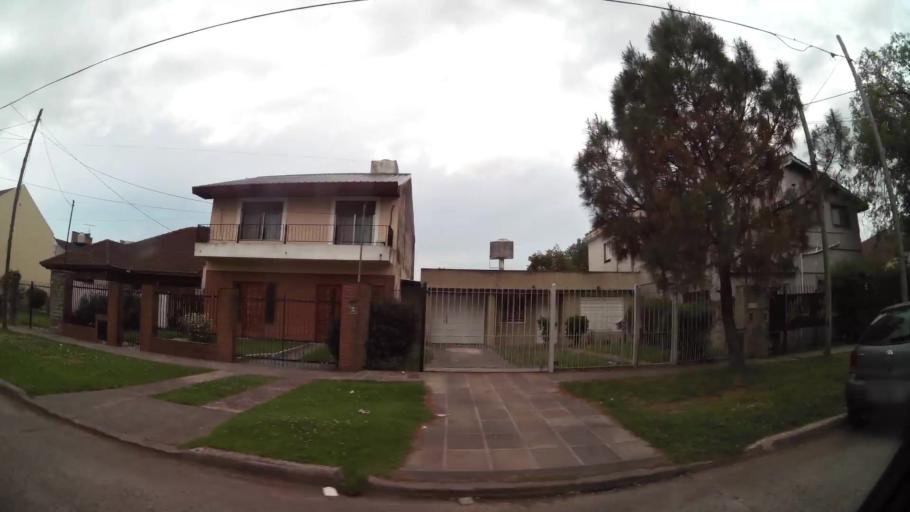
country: AR
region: Buenos Aires
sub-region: Partido de Tigre
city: Tigre
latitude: -34.4665
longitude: -58.6502
